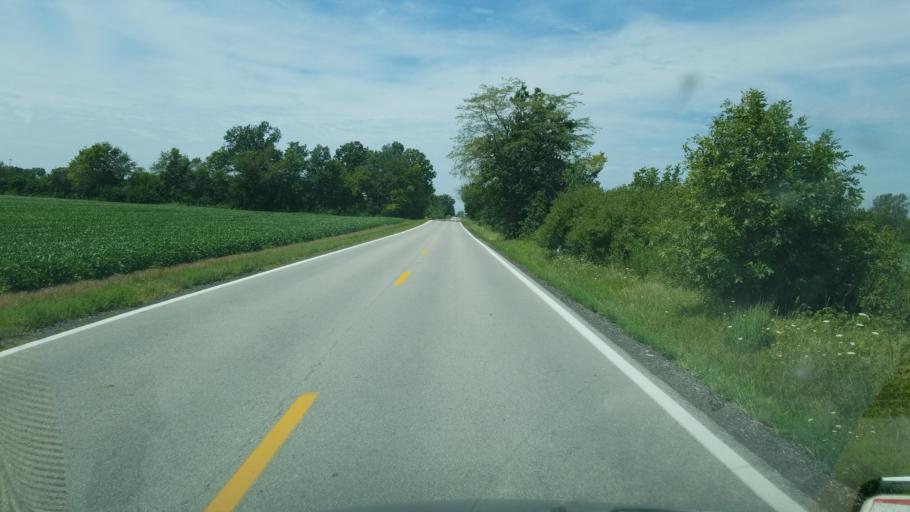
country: US
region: Ohio
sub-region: Madison County
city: West Jefferson
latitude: 39.8638
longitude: -83.2612
